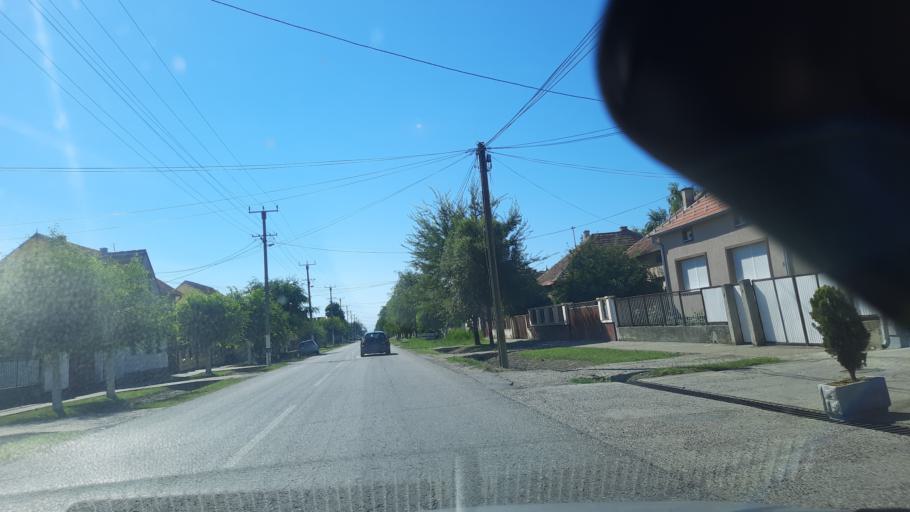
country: RS
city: Simanovci
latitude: 44.8747
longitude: 20.0880
